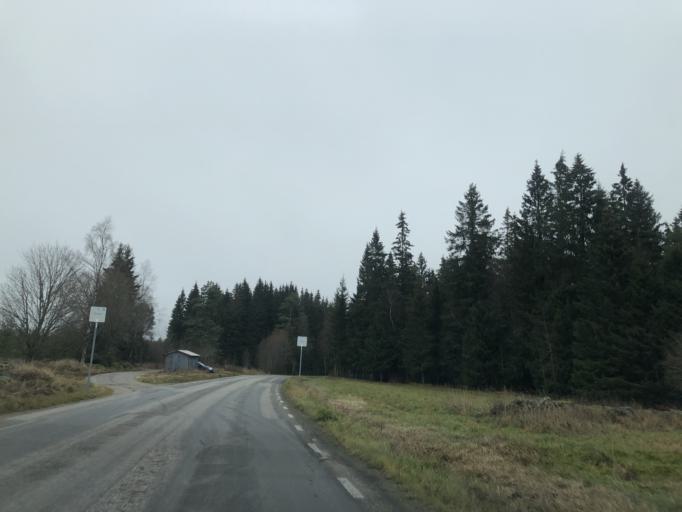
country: SE
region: Vaestra Goetaland
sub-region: Ulricehamns Kommun
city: Ulricehamn
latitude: 57.6895
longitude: 13.4768
